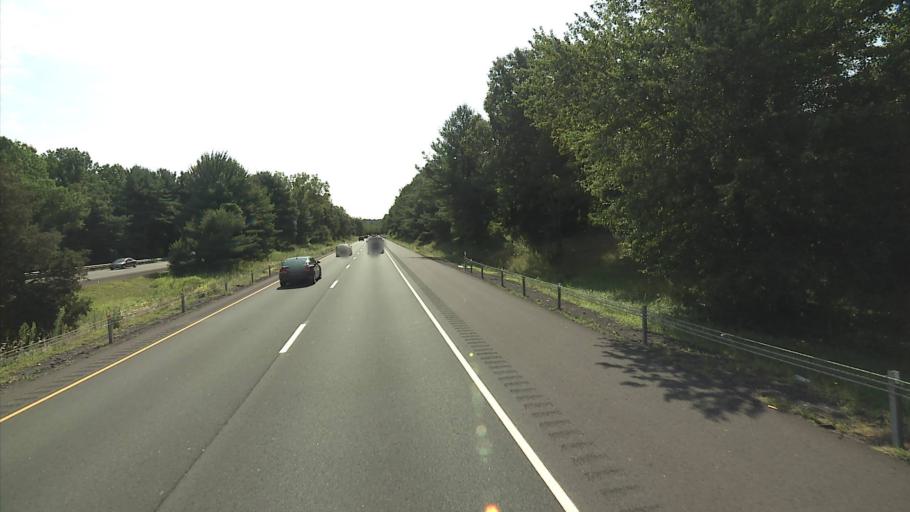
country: US
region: Connecticut
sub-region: Hartford County
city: Glastonbury Center
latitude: 41.7073
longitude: -72.5790
